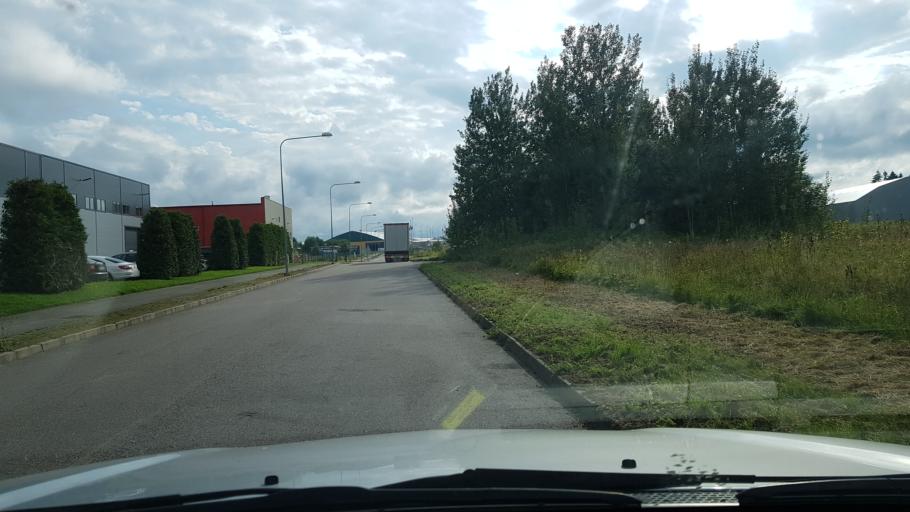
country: EE
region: Harju
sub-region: Rae vald
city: Jueri
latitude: 59.3714
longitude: 24.8788
